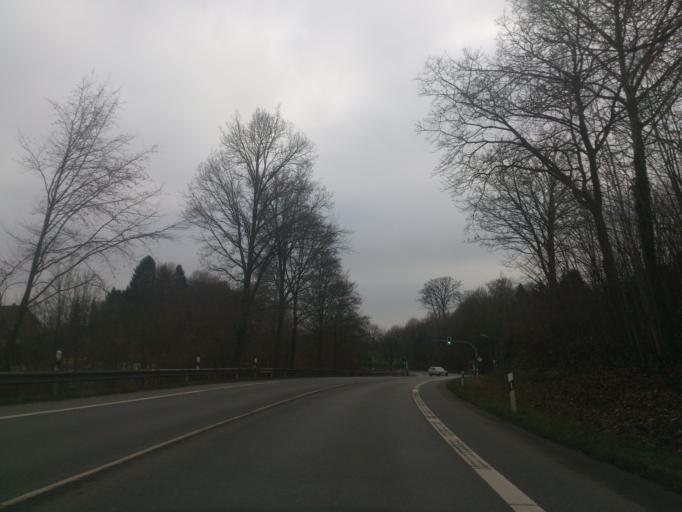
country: DE
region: North Rhine-Westphalia
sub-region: Regierungsbezirk Detmold
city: Vlotho
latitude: 52.1479
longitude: 8.8391
